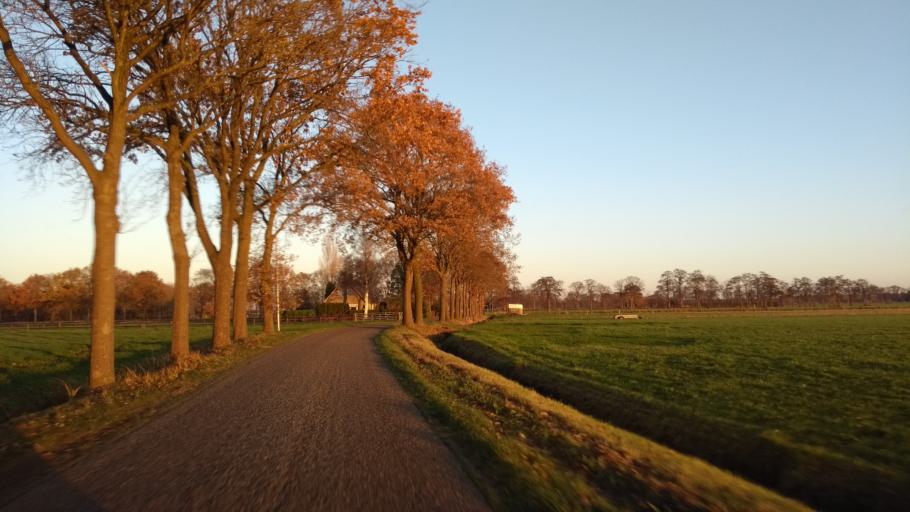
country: NL
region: Overijssel
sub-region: Gemeente Staphorst
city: Staphorst
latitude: 52.6021
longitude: 6.3007
